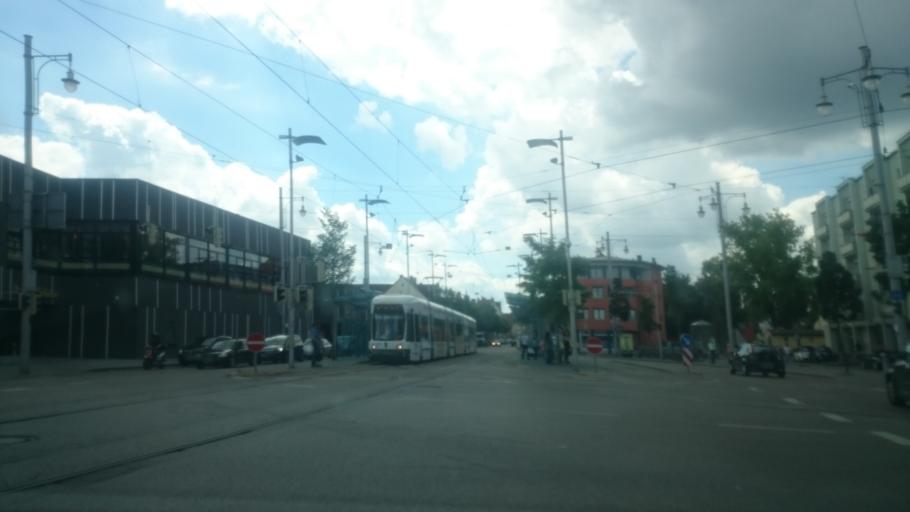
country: DE
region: Bavaria
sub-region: Swabia
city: Augsburg
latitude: 48.3858
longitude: 10.8806
